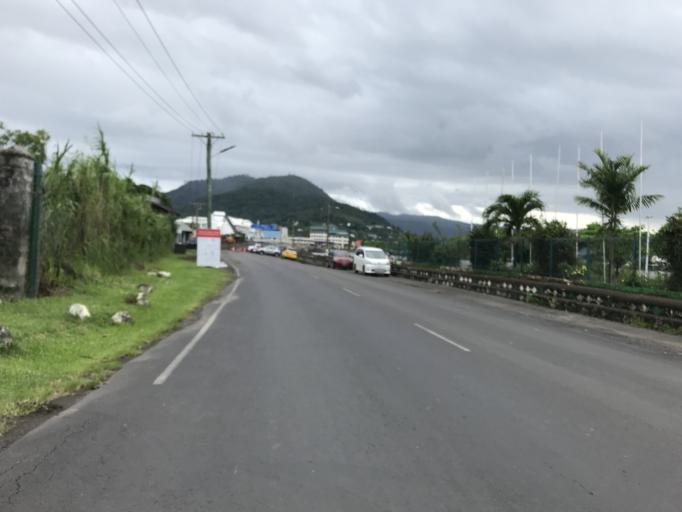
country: WS
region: Tuamasaga
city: Apia
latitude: -13.8291
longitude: -171.7593
